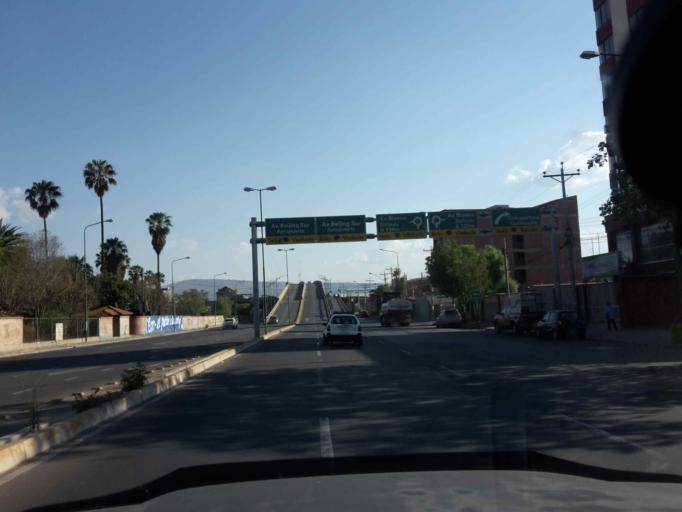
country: BO
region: Cochabamba
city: Cochabamba
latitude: -17.3907
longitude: -66.1835
